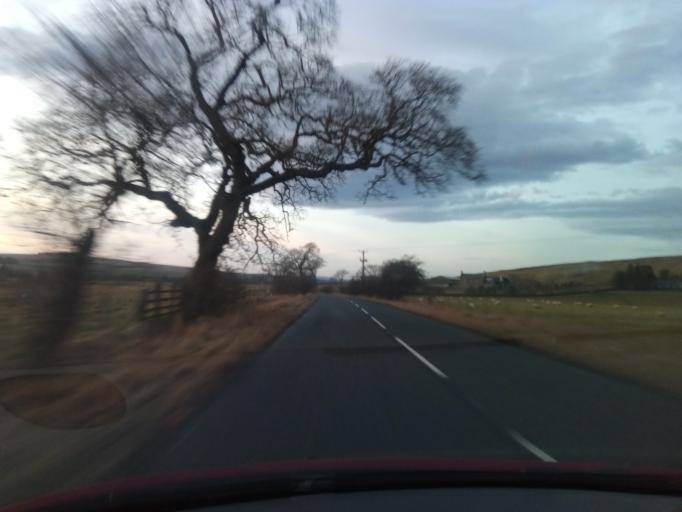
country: GB
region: England
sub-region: Northumberland
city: Otterburn
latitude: 55.2386
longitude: -2.2019
